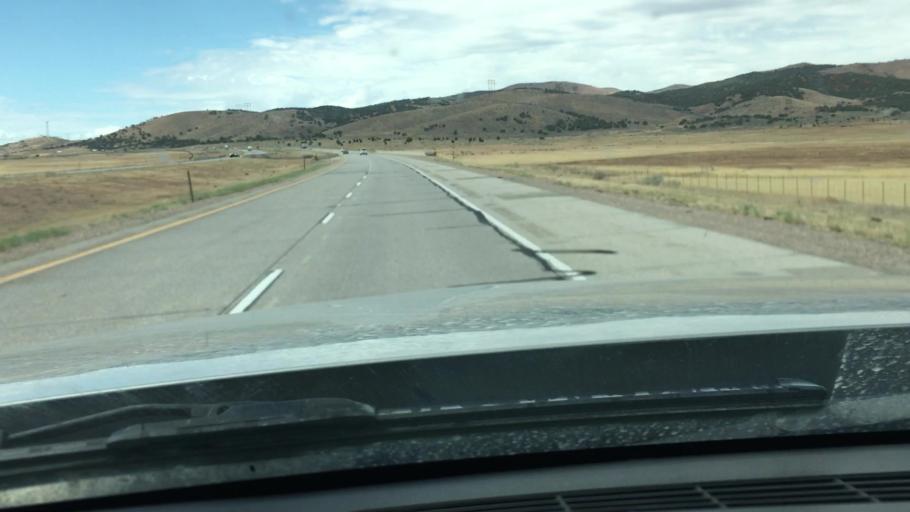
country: US
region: Utah
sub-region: Juab County
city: Nephi
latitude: 39.6546
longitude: -111.8920
